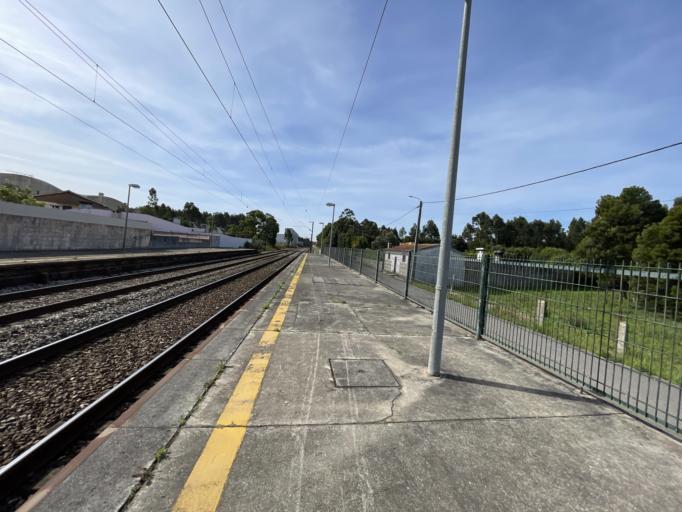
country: PT
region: Aveiro
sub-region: Ovar
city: Cortegaca
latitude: 40.9403
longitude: -8.6301
